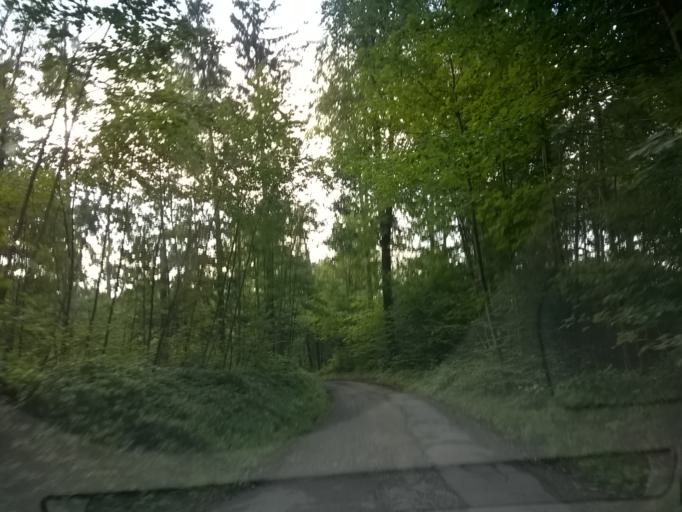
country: CH
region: Zurich
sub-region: Bezirk Buelach
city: Bachenbulach
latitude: 47.4997
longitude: 8.5653
